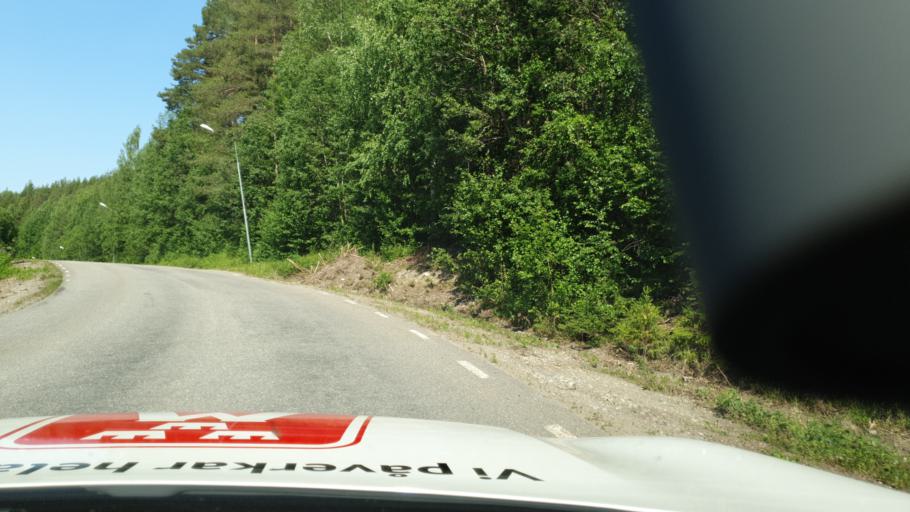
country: SE
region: Vaesterbotten
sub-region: Skelleftea Kommun
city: Langsele
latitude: 64.9396
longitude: 20.0038
